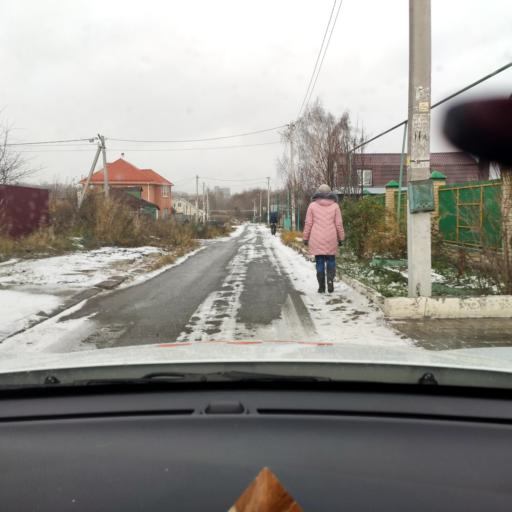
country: RU
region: Tatarstan
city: Verkhniy Uslon
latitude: 55.8002
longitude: 49.0371
